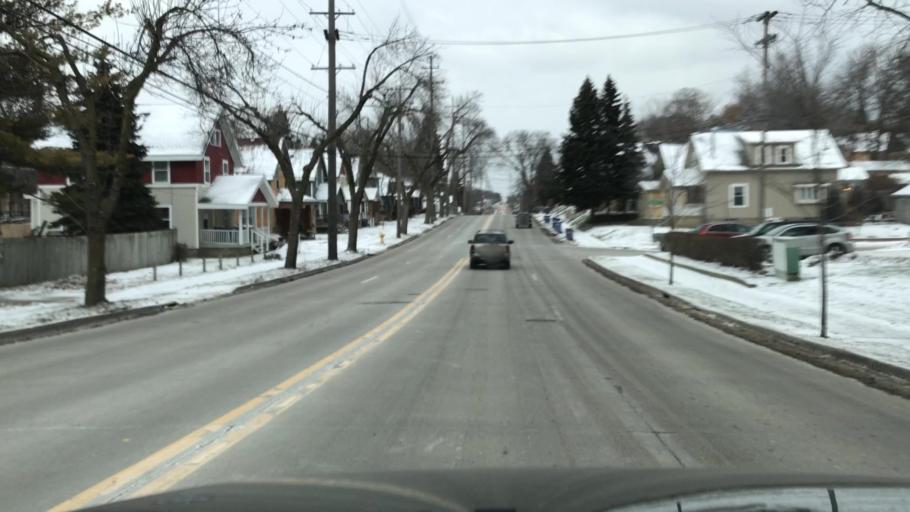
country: US
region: Michigan
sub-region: Kent County
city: Grand Rapids
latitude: 42.9633
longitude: -85.6397
